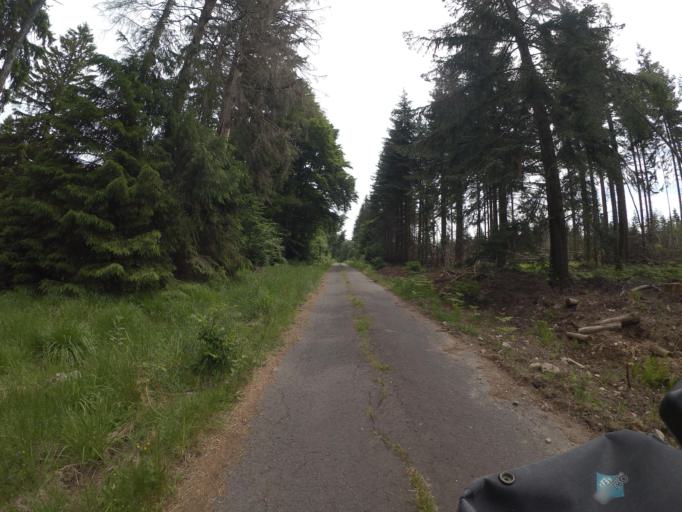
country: DE
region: Rheinland-Pfalz
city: Zusch
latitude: 49.6854
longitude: 7.0319
